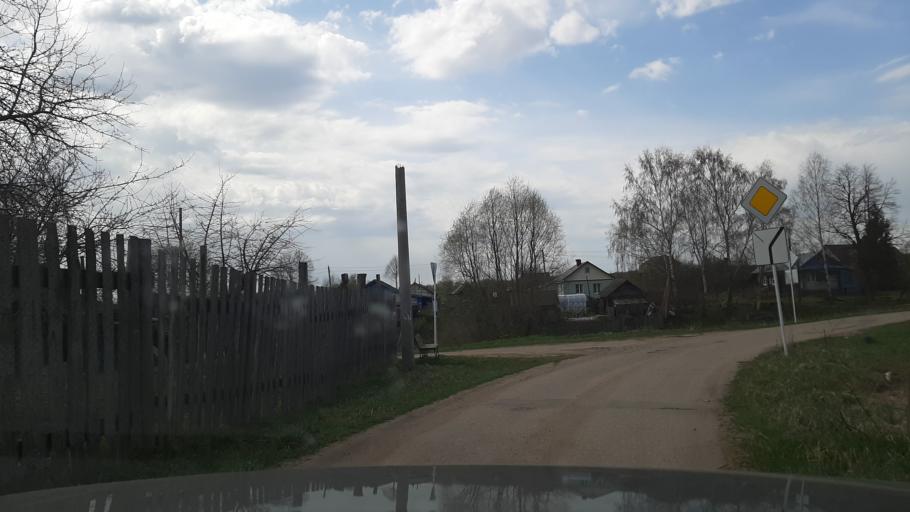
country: RU
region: Ivanovo
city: Furmanov
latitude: 57.3173
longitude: 41.1608
